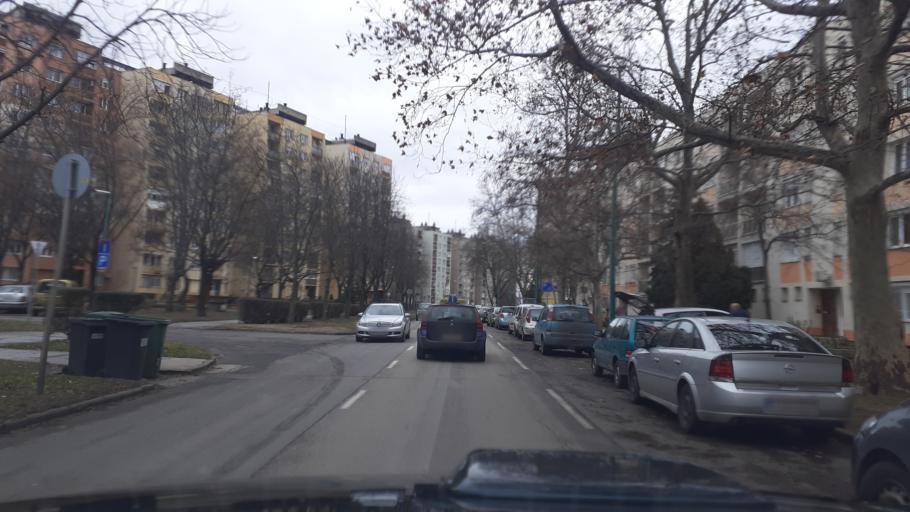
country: HU
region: Fejer
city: dunaujvaros
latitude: 46.9721
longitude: 18.9363
